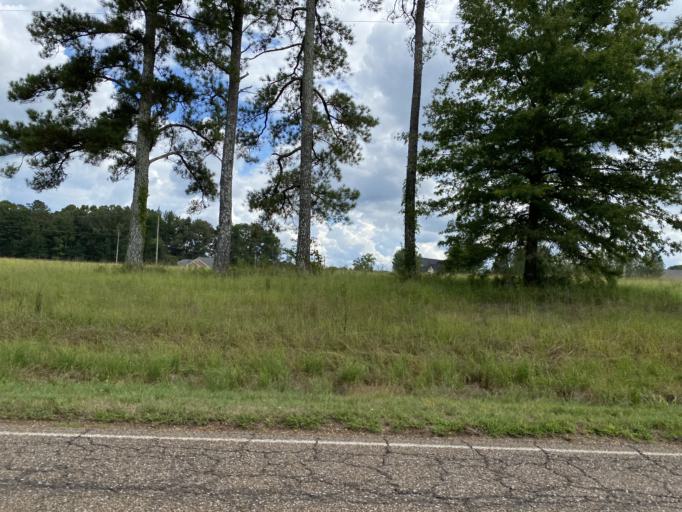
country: US
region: Mississippi
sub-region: Monroe County
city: Amory
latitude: 33.9745
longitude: -88.4434
